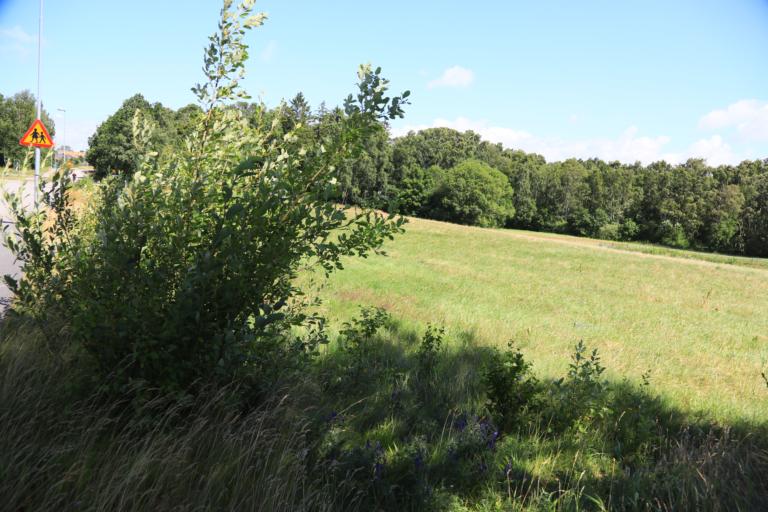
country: SE
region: Halland
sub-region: Varbergs Kommun
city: Traslovslage
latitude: 57.0998
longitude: 12.2977
